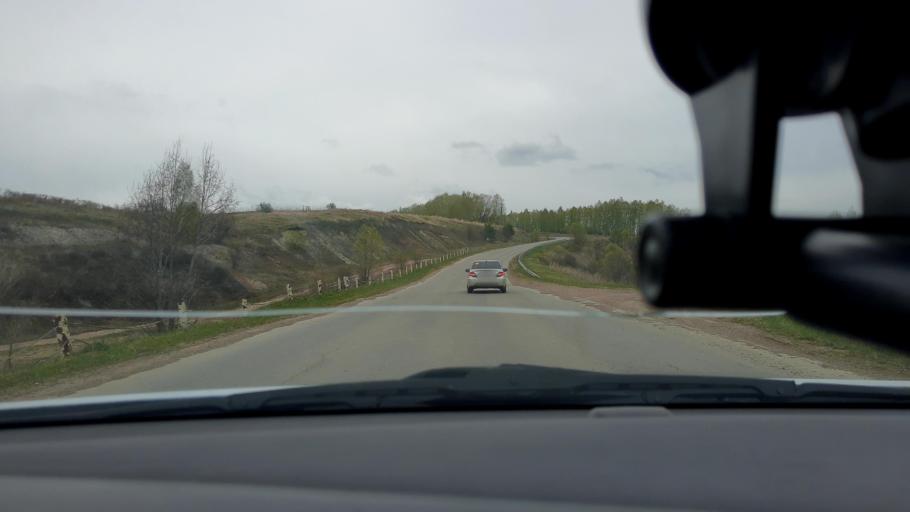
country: RU
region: Bashkortostan
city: Yazykovo
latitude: 55.1343
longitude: 56.0818
